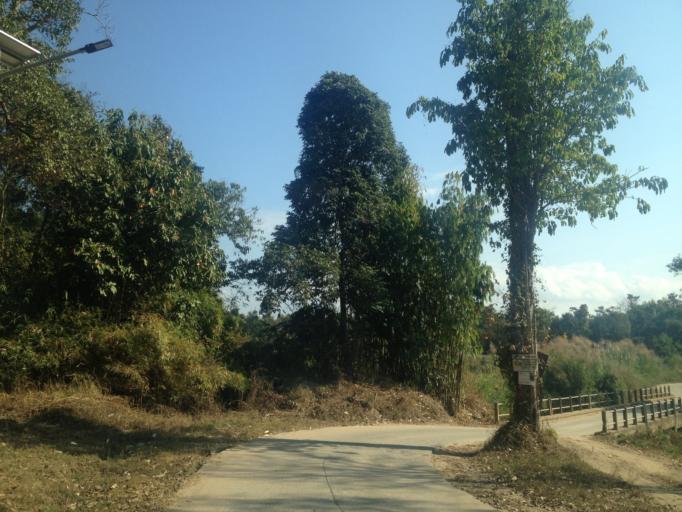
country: TH
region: Mae Hong Son
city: Ban Huai I Huak
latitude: 18.0971
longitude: 98.2090
